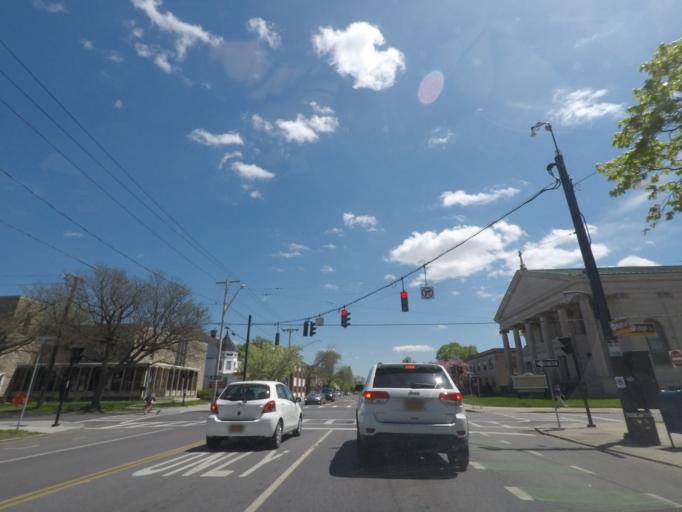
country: US
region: New York
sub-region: Albany County
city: West Albany
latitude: 42.6620
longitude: -73.7844
